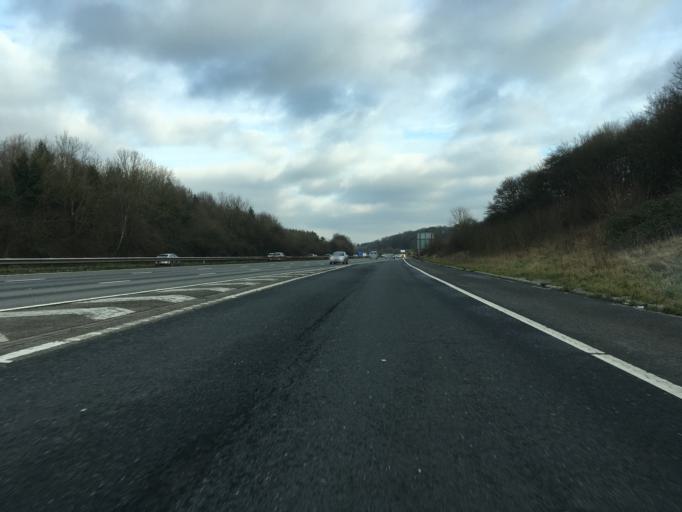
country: GB
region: England
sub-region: South Gloucestershire
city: Falfield
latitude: 51.6384
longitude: -2.4497
